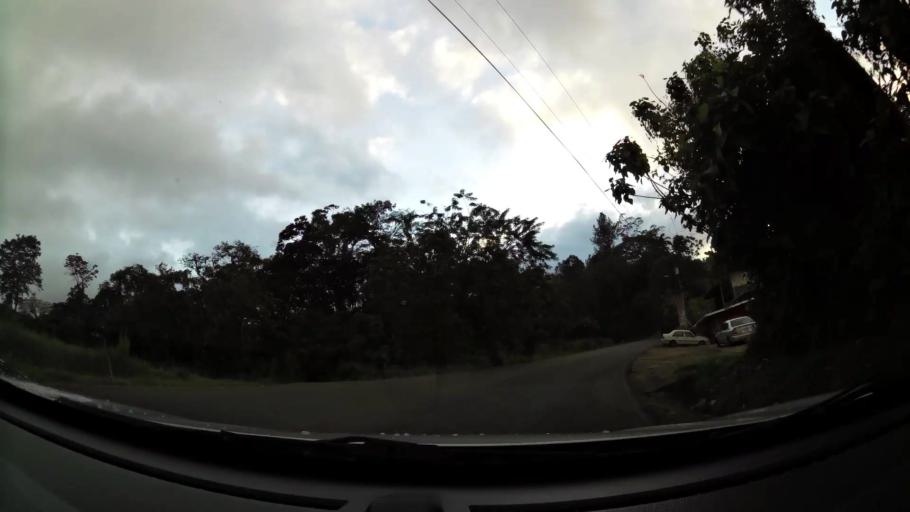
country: CR
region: Cartago
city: Turrialba
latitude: 9.9007
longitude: -83.6883
